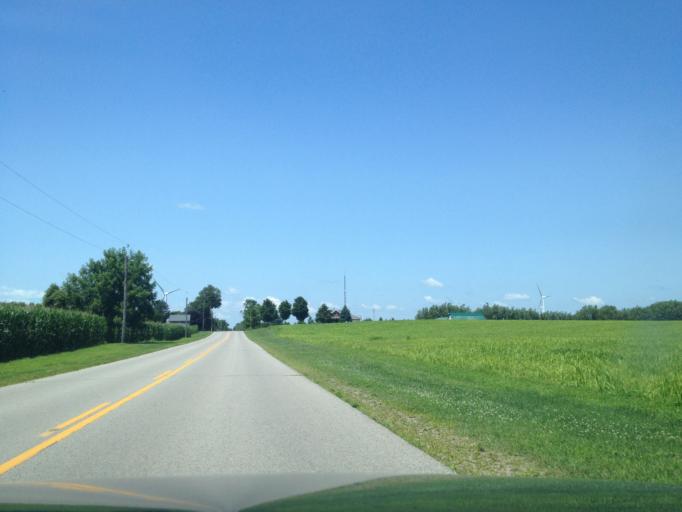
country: CA
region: Ontario
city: Aylmer
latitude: 42.6095
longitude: -80.6846
